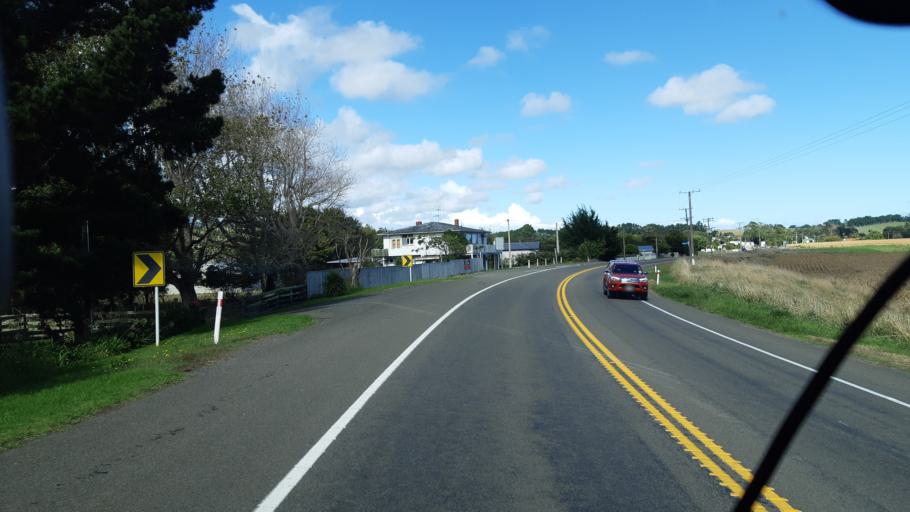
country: NZ
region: Manawatu-Wanganui
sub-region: Wanganui District
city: Wanganui
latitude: -40.0348
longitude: 175.2114
